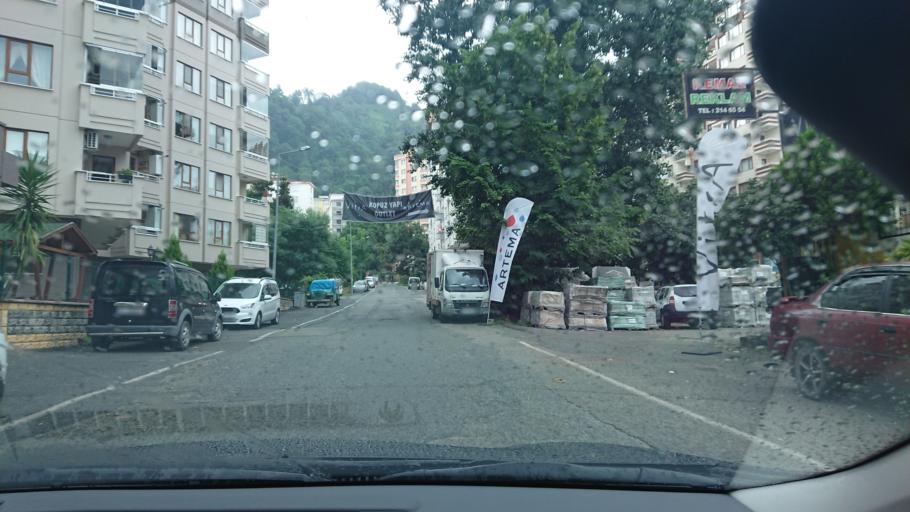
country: TR
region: Rize
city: Rize
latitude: 41.0264
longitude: 40.5462
